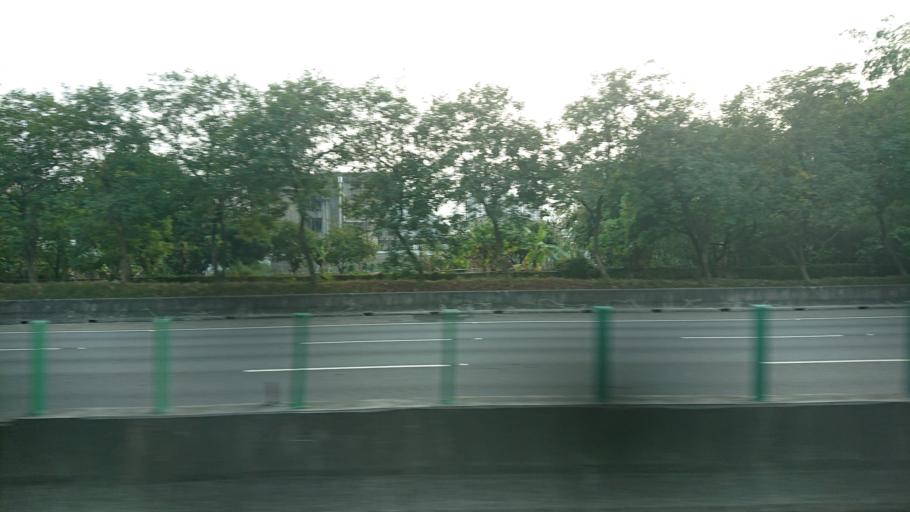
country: TW
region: Taiwan
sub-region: Changhua
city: Chang-hua
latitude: 24.1164
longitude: 120.5918
